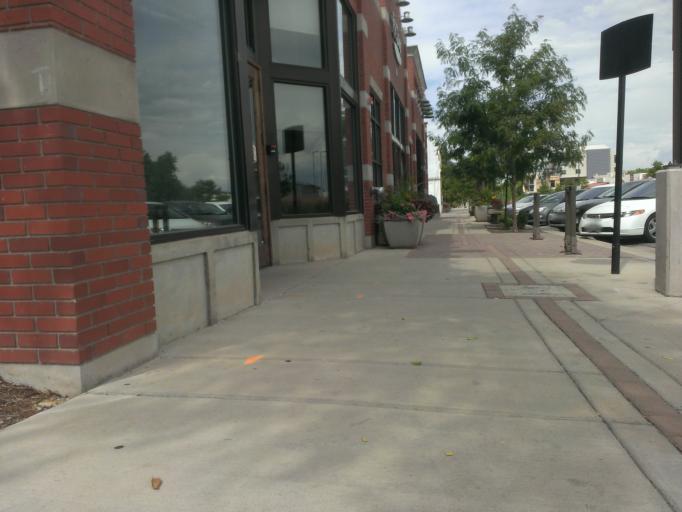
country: US
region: Colorado
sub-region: Larimer County
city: Fort Collins
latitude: 40.5894
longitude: -105.0740
